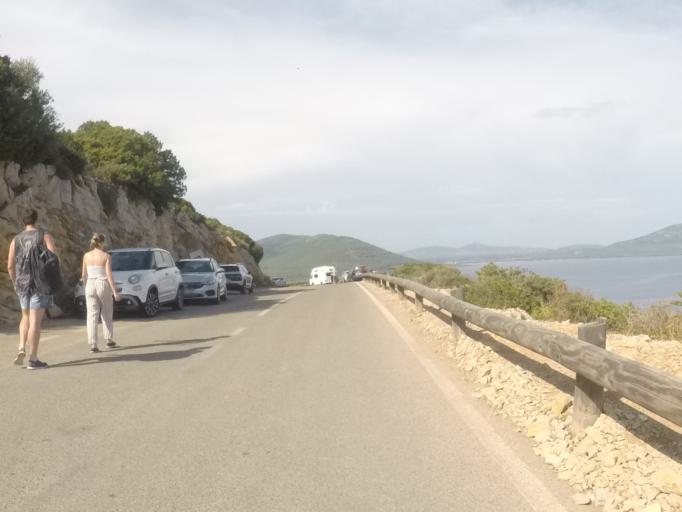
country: IT
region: Sardinia
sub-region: Provincia di Sassari
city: Alghero
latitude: 40.5648
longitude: 8.1644
